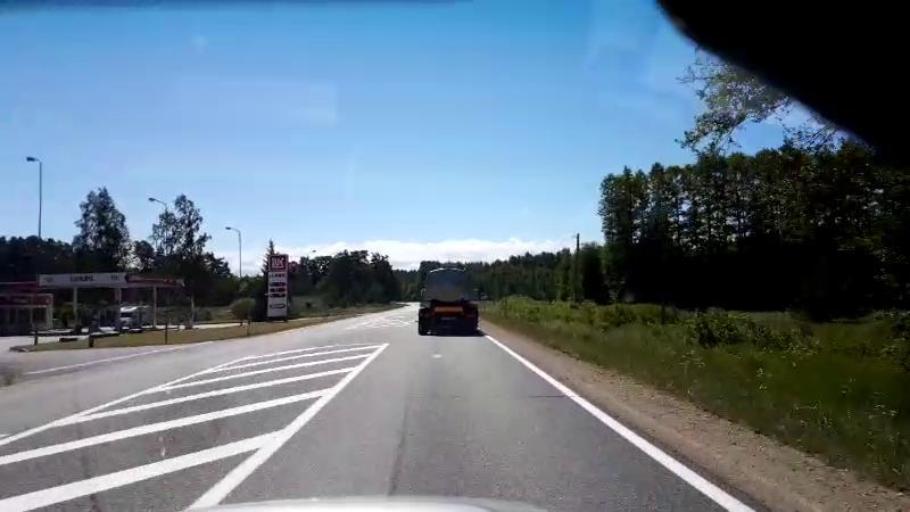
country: LV
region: Saulkrastu
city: Saulkrasti
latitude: 57.3863
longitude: 24.4292
